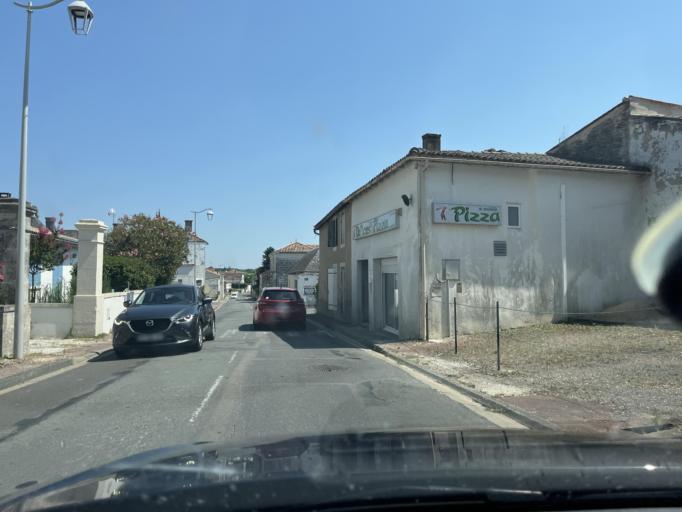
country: FR
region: Poitou-Charentes
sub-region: Departement de la Charente-Maritime
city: Mortagne-sur-Gironde
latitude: 45.4569
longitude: -0.6903
